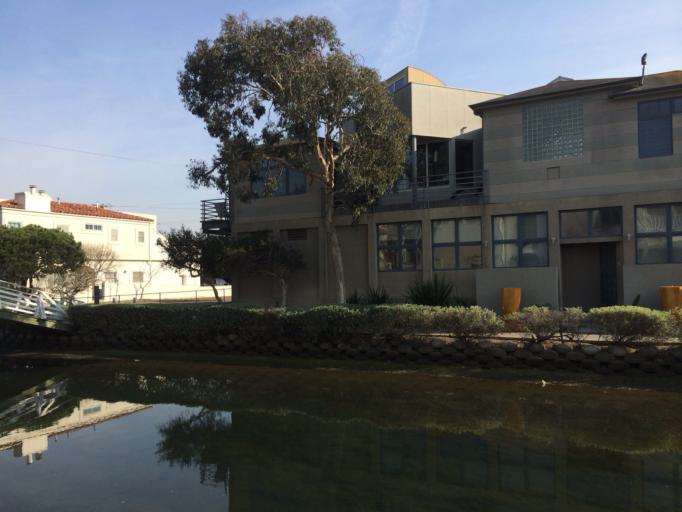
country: US
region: California
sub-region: Los Angeles County
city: Marina del Rey
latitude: 33.9840
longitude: -118.4678
